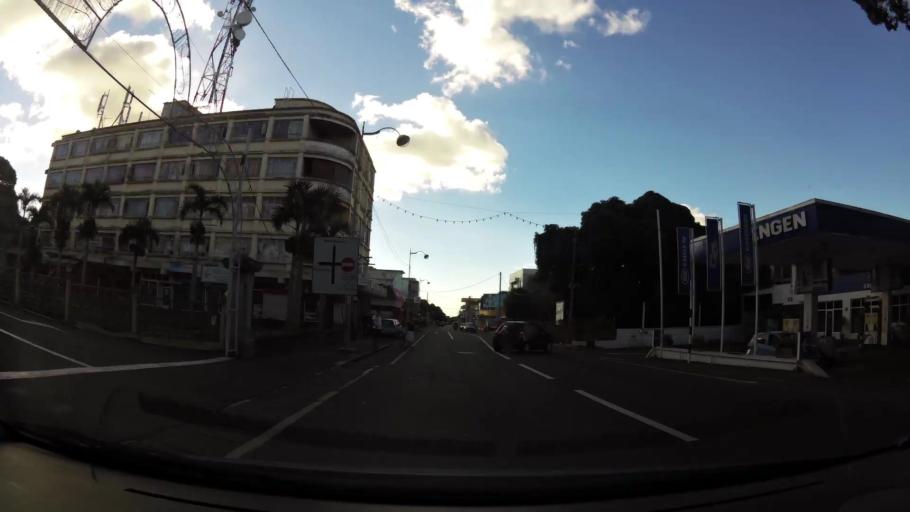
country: MU
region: Plaines Wilhems
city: Ebene
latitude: -20.2393
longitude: 57.4723
